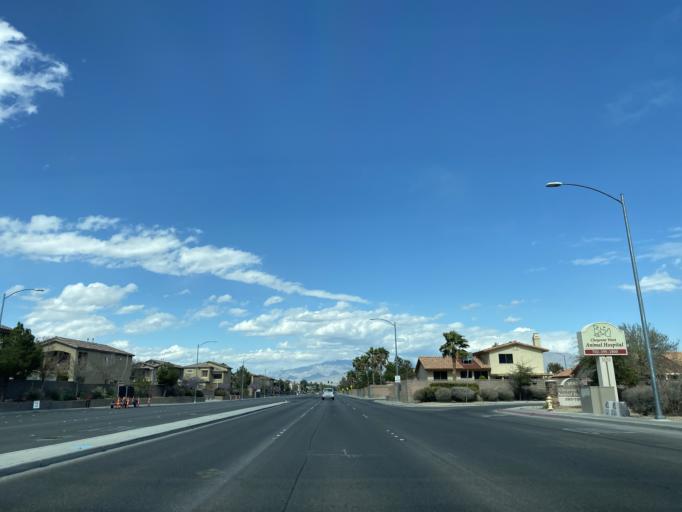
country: US
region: Nevada
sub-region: Clark County
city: Spring Valley
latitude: 36.2260
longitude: -115.2605
